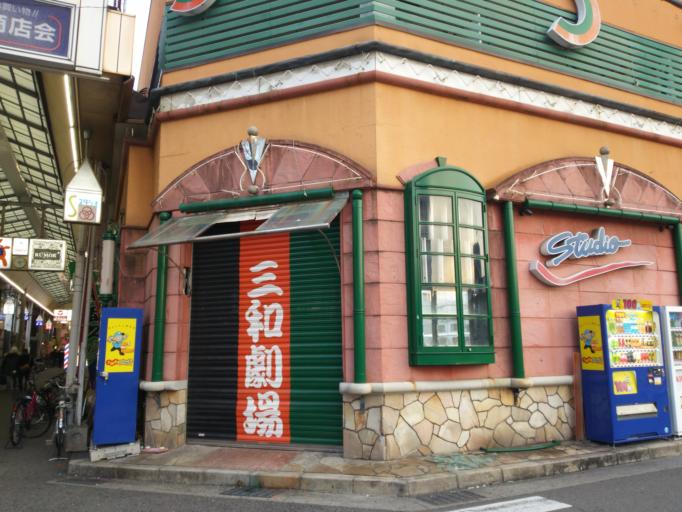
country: JP
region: Hyogo
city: Amagasaki
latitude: 34.7213
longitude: 135.4080
